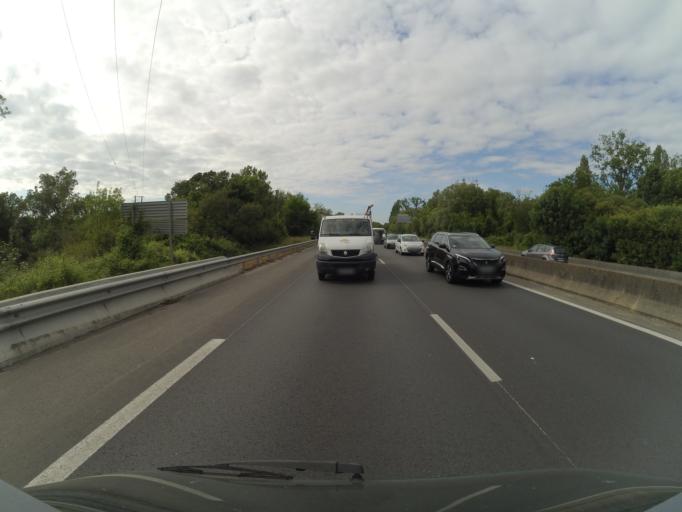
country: FR
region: Poitou-Charentes
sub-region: Departement de la Charente-Maritime
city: Aytre
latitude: 46.1483
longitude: -1.1108
